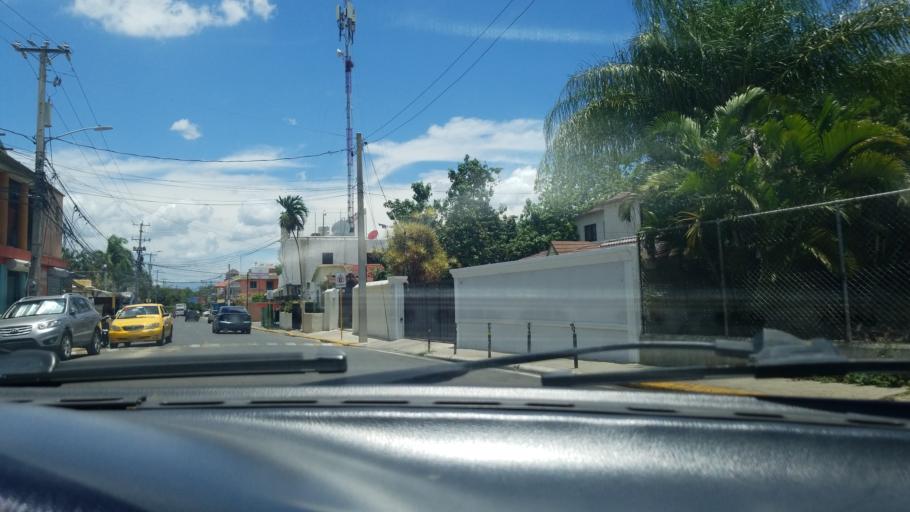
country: DO
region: Santiago
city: Santiago de los Caballeros
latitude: 19.4773
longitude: -70.6849
